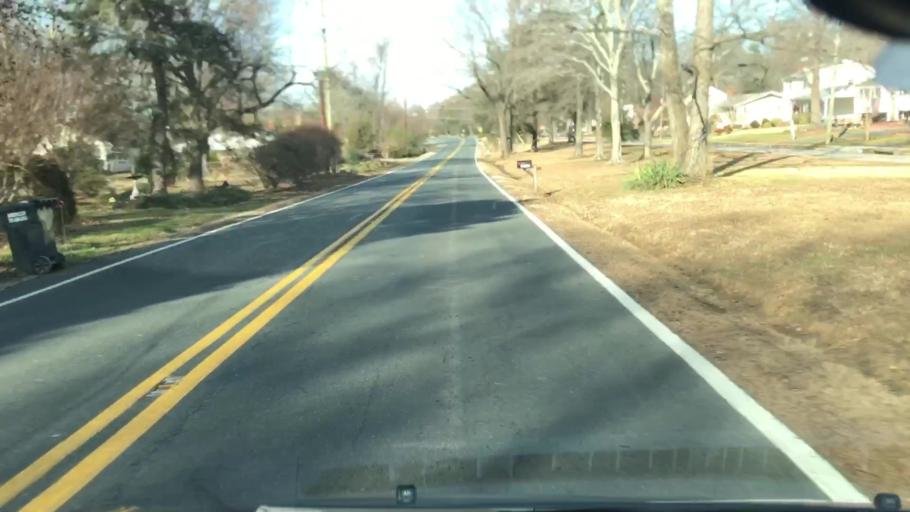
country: US
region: Virginia
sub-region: Fairfax County
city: Mount Vernon
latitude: 38.7254
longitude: -77.0907
